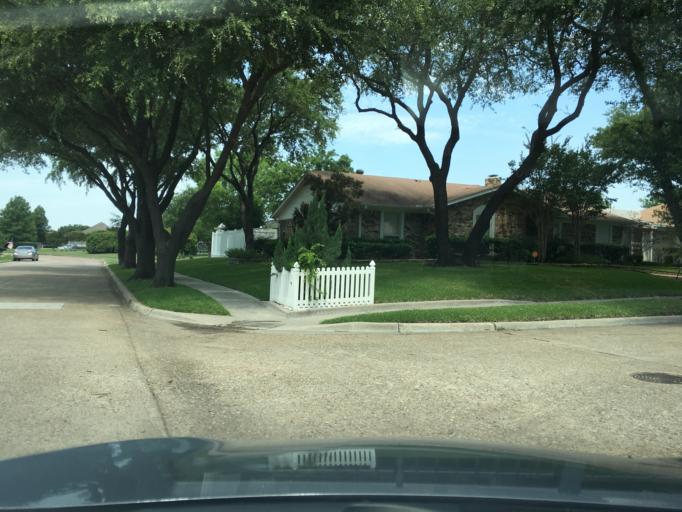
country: US
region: Texas
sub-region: Dallas County
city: Richardson
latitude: 32.9662
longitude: -96.6970
